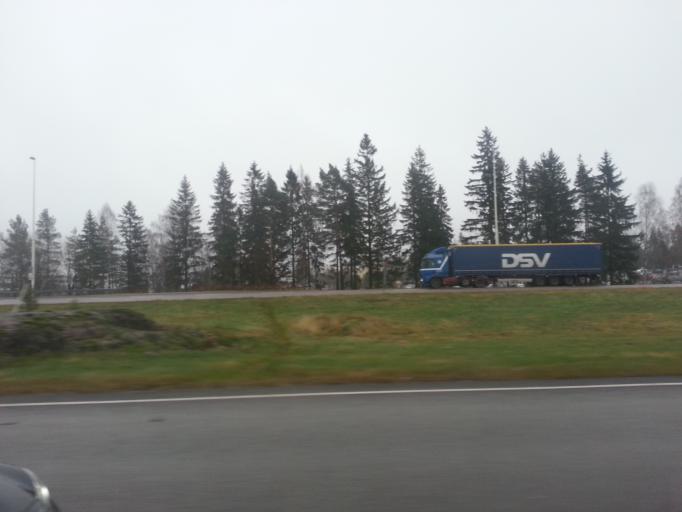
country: FI
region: Uusimaa
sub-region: Helsinki
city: Vantaa
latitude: 60.3104
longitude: 24.9685
